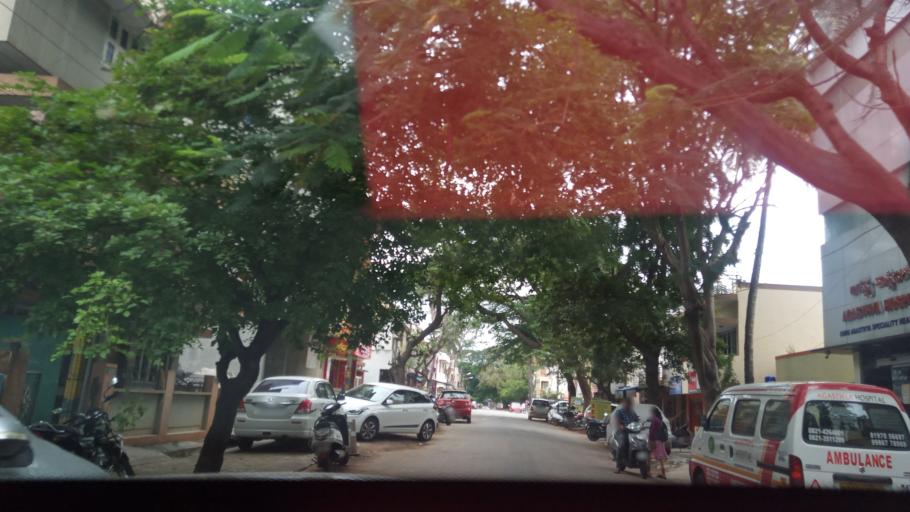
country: IN
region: Karnataka
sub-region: Mysore
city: Mysore
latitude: 12.3018
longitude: 76.6280
